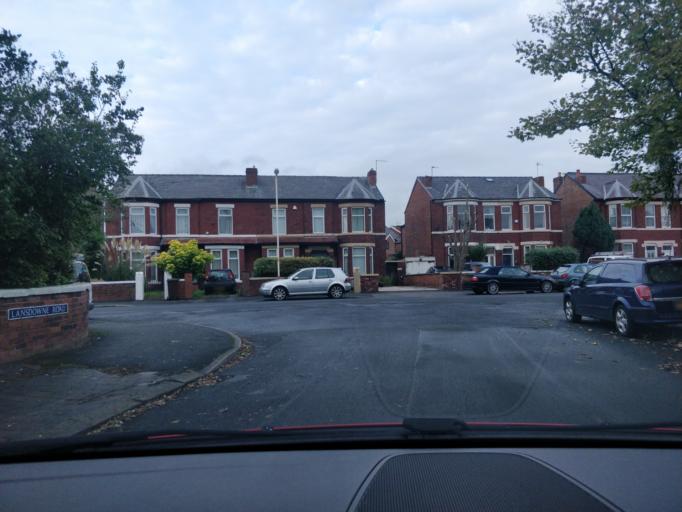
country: GB
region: England
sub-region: Sefton
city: Southport
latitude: 53.6450
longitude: -2.9805
